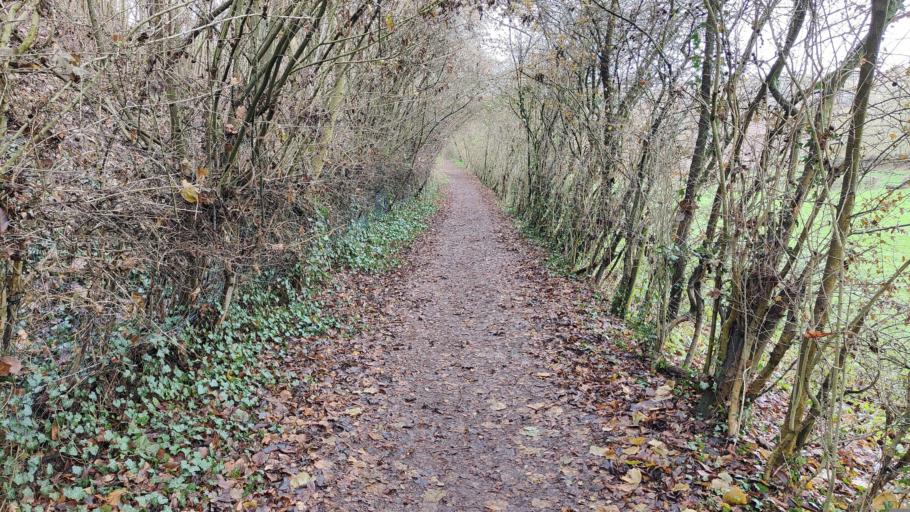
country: NL
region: Limburg
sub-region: Valkenburg aan de Geul
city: Berg
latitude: 50.8336
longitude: 5.7682
